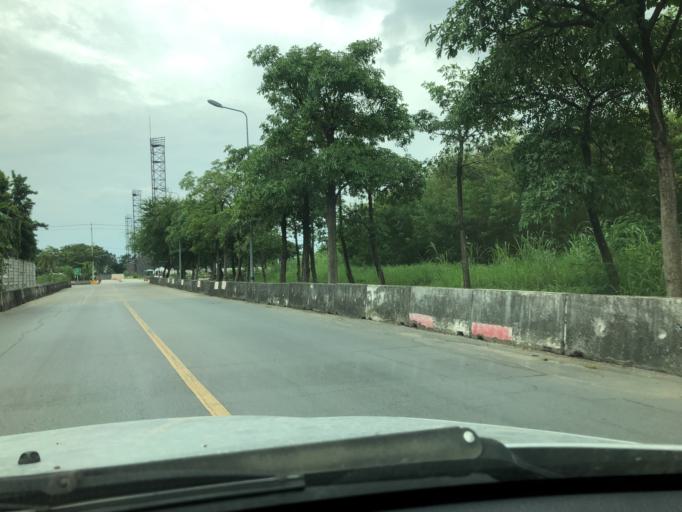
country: TH
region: Nonthaburi
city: Pak Kret
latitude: 13.9290
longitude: 100.5393
